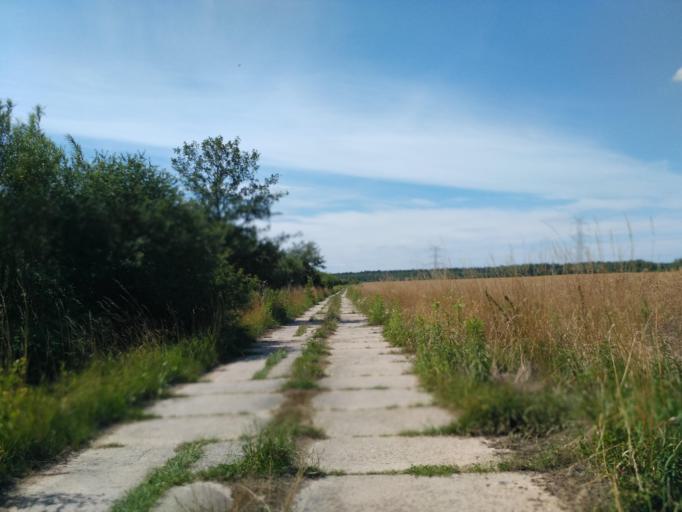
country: PL
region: Subcarpathian Voivodeship
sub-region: Powiat brzozowski
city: Haczow
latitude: 49.6536
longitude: 21.8653
